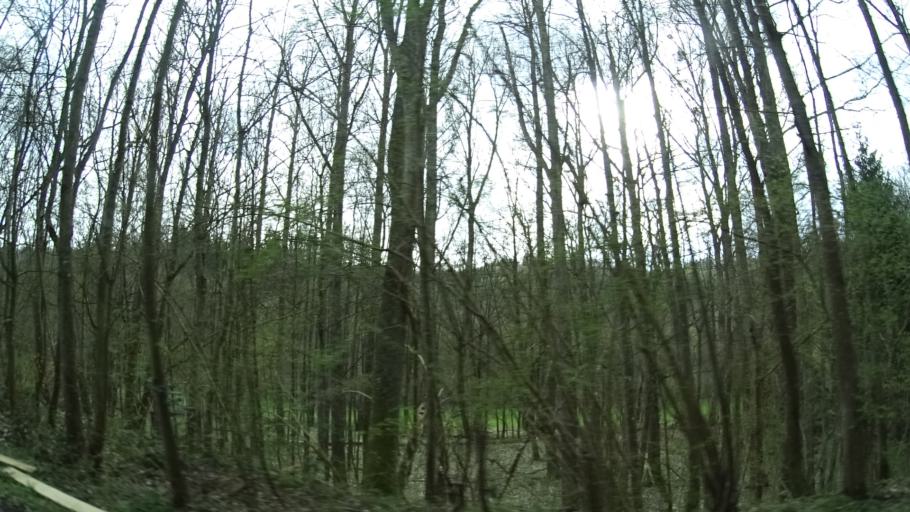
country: DE
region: Rheinland-Pfalz
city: Bockenau
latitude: 49.8400
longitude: 7.6670
